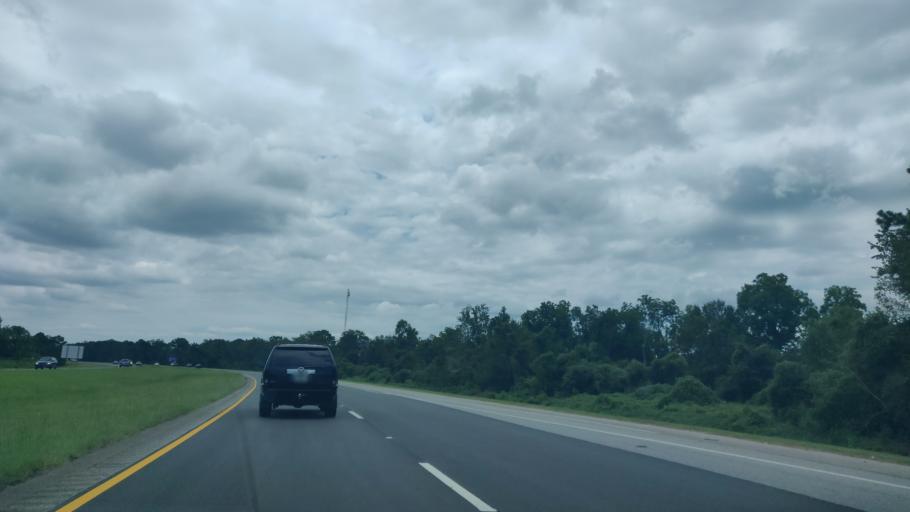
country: US
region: Georgia
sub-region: Dougherty County
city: Albany
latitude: 31.6153
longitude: -84.1973
